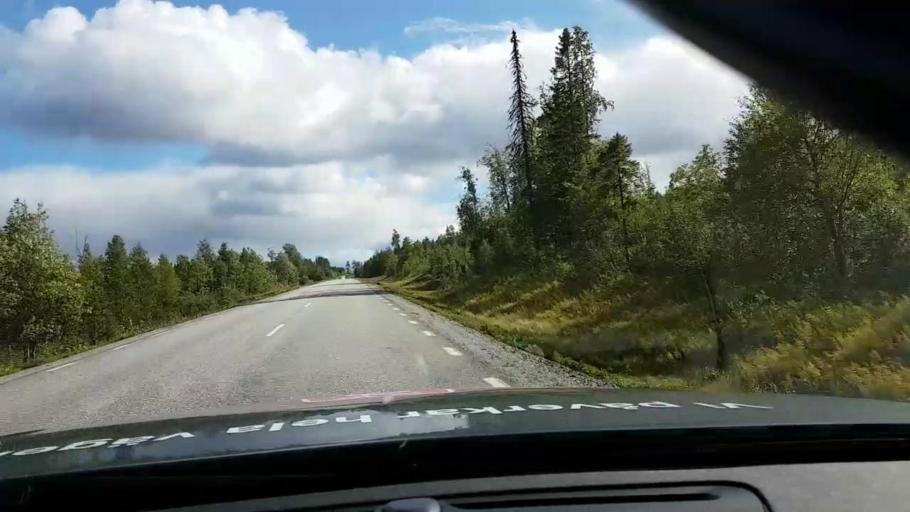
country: SE
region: Vaesterbotten
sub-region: Asele Kommun
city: Asele
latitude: 63.7778
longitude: 17.6689
